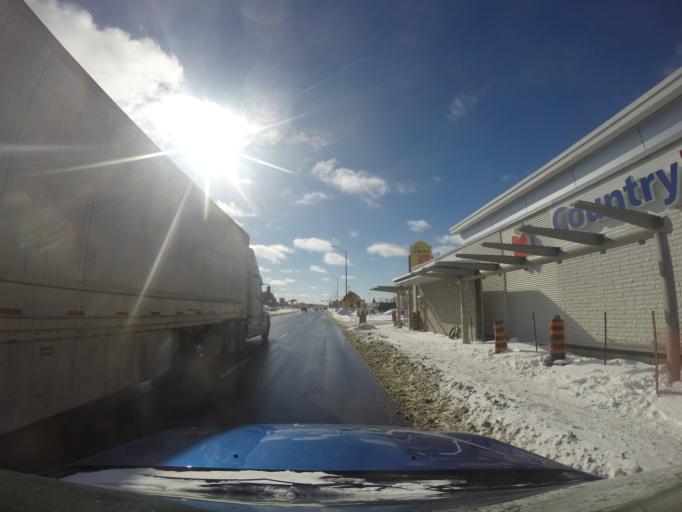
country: CA
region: Ontario
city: Cambridge
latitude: 43.4076
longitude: -80.3282
